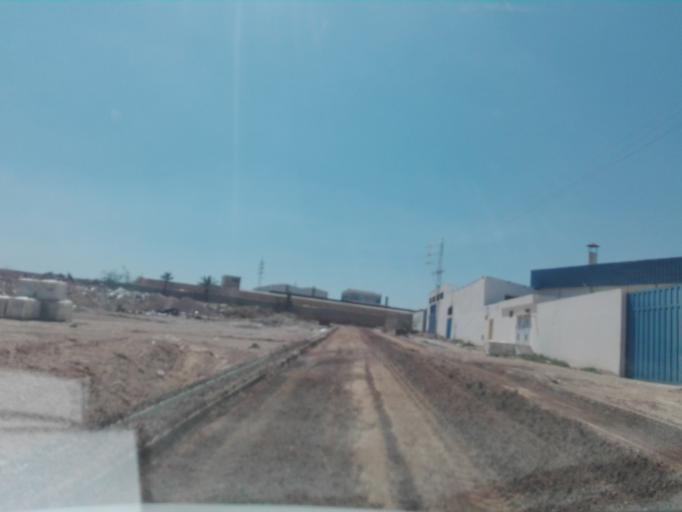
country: TN
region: Safaqis
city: Sfax
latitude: 34.7262
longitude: 10.5171
